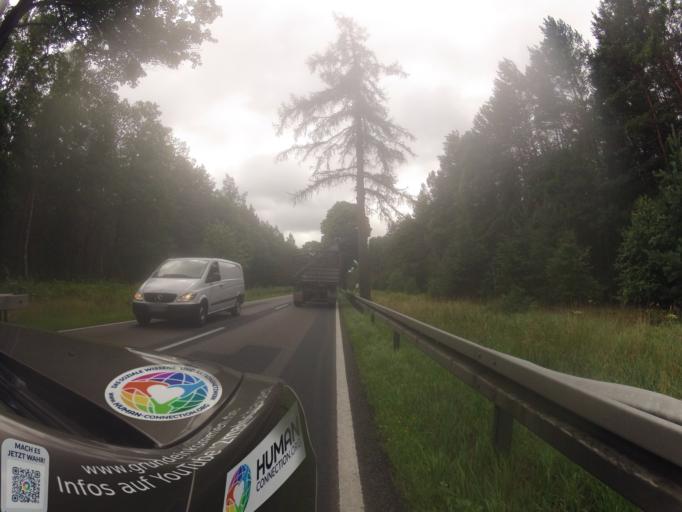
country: DE
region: Mecklenburg-Vorpommern
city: Jatznick
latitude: 53.6271
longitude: 13.9284
